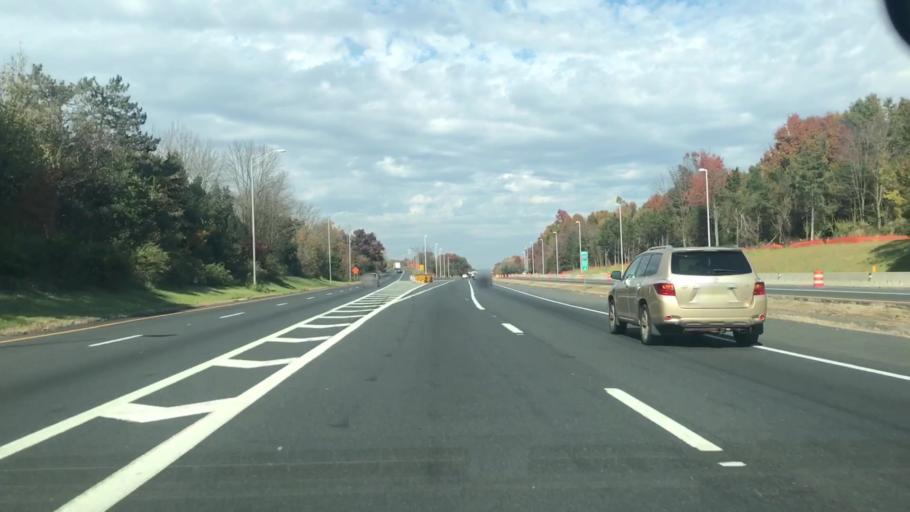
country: US
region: New Jersey
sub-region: Somerset County
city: Bridgewater
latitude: 40.6341
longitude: -74.6435
